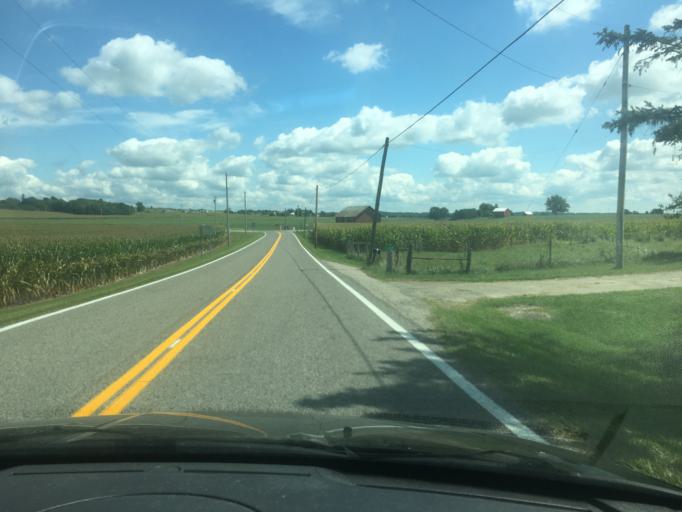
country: US
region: Ohio
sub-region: Logan County
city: West Liberty
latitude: 40.2296
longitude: -83.7096
